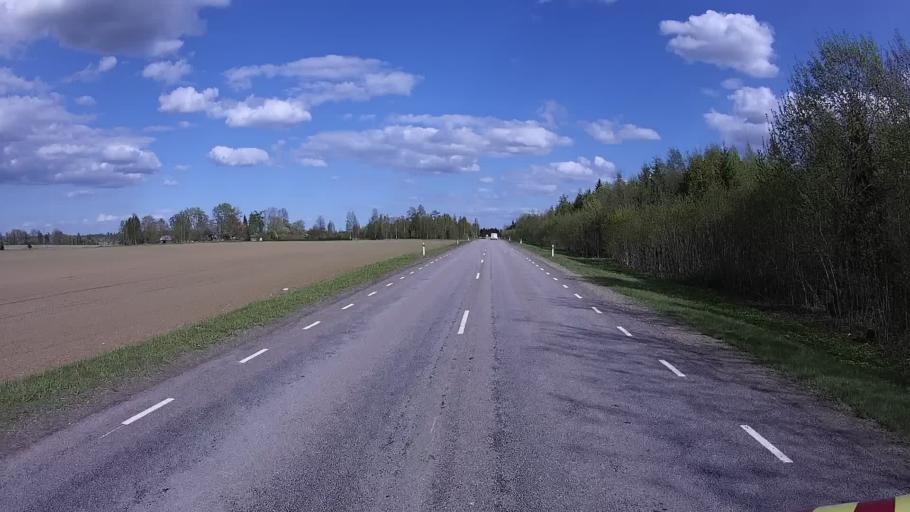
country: EE
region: Tartu
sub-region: Alatskivi vald
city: Kallaste
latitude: 58.5276
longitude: 27.0387
